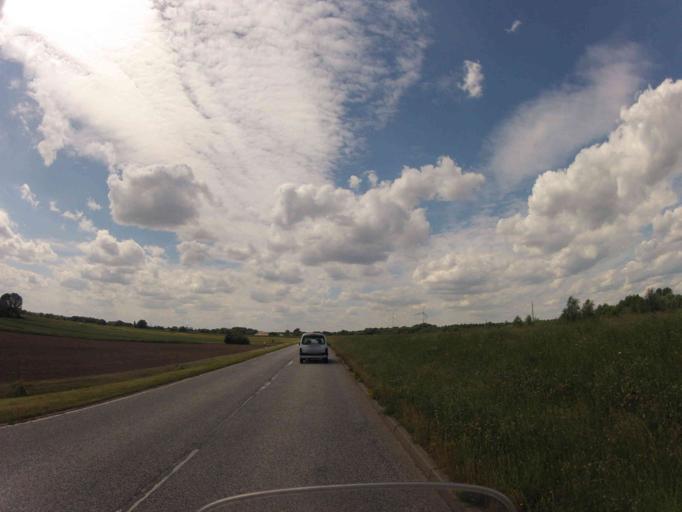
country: DE
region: Hamburg
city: Rothenburgsort
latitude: 53.4998
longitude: 10.0627
